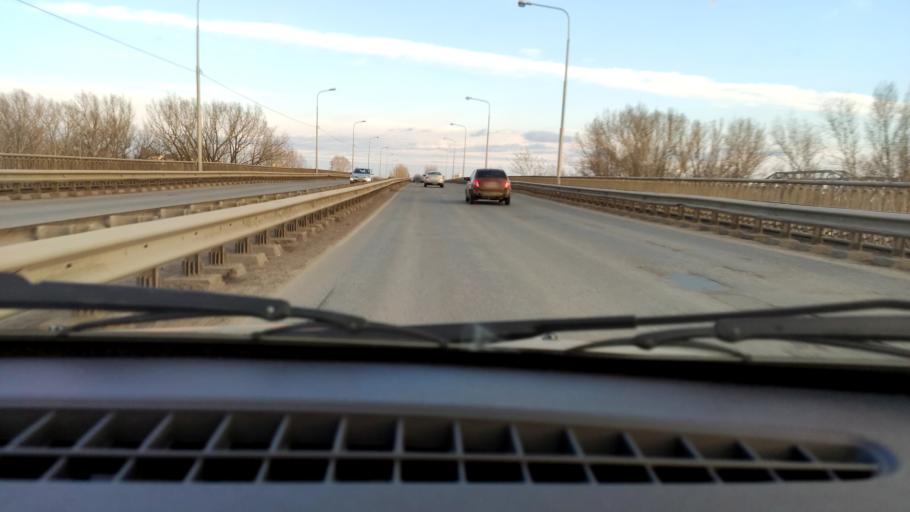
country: RU
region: Bashkortostan
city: Iglino
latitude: 54.7874
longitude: 56.2150
